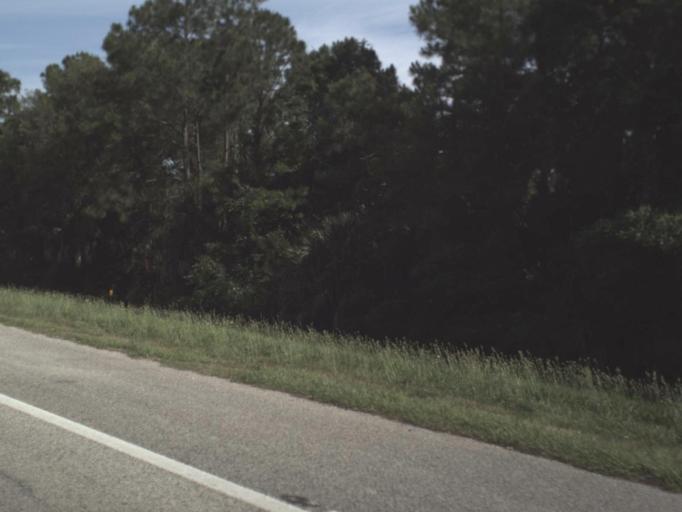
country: US
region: Florida
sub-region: Saint Johns County
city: Ponte Vedra Beach
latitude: 30.2580
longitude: -81.4044
